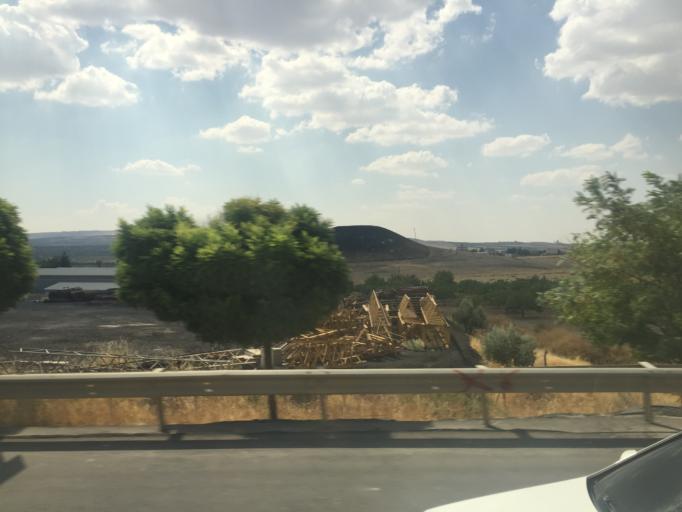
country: TR
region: Sanliurfa
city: Sanliurfa
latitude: 37.2557
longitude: 38.7927
